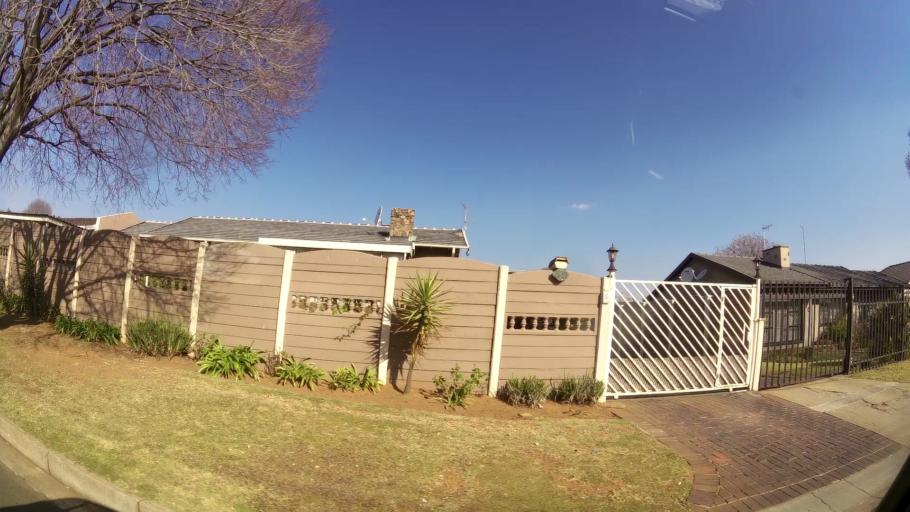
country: ZA
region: Gauteng
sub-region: City of Johannesburg Metropolitan Municipality
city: Johannesburg
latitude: -26.2554
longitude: 28.0006
